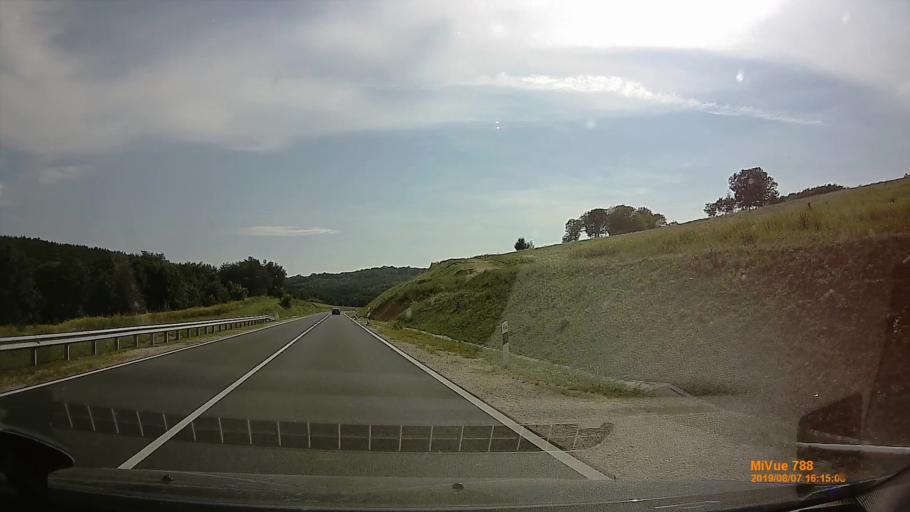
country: HU
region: Zala
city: Zalalovo
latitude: 46.8283
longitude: 16.6016
